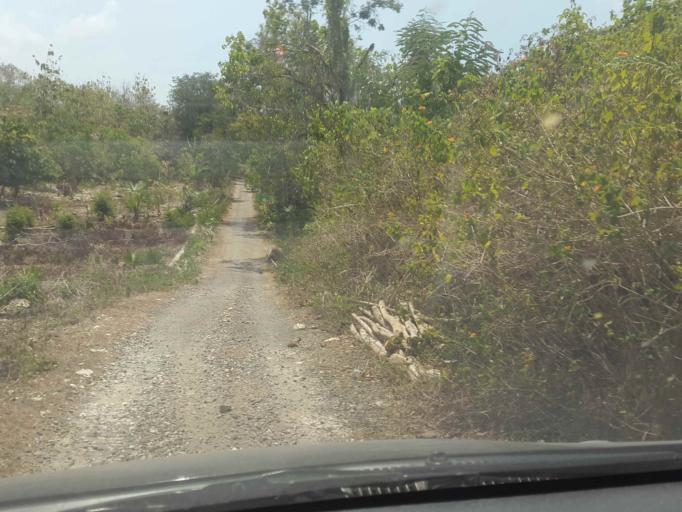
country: ID
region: South Sulawesi
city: Bantaeng
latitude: -6.1680
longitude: 120.4497
